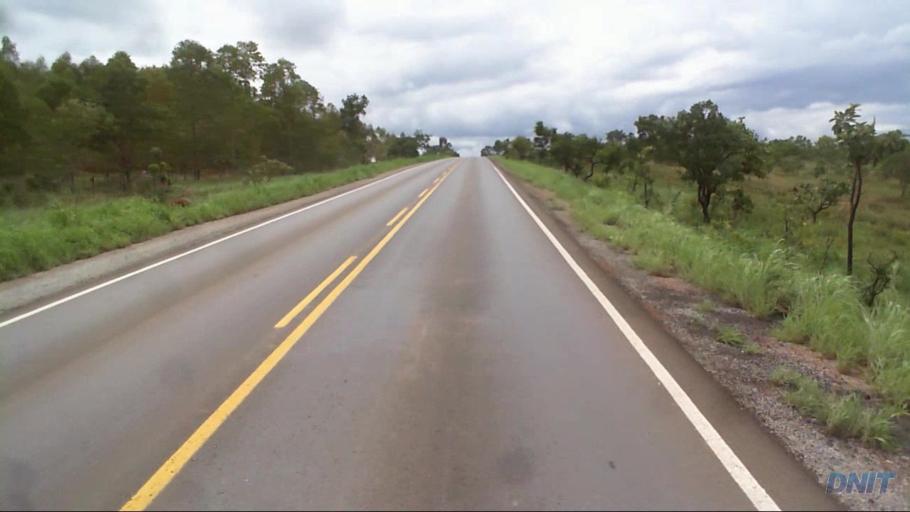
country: BR
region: Goias
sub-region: Padre Bernardo
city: Padre Bernardo
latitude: -15.3798
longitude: -48.2125
